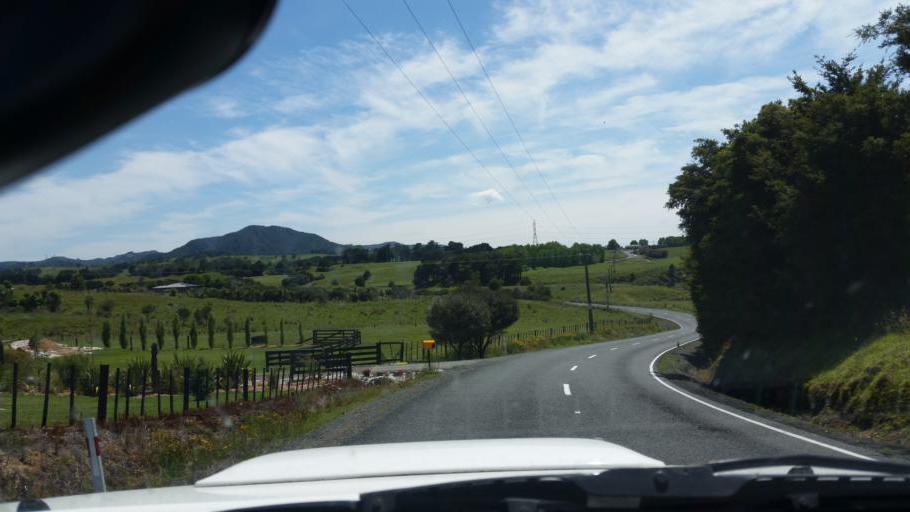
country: NZ
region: Auckland
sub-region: Auckland
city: Wellsford
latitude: -36.1697
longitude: 174.4208
